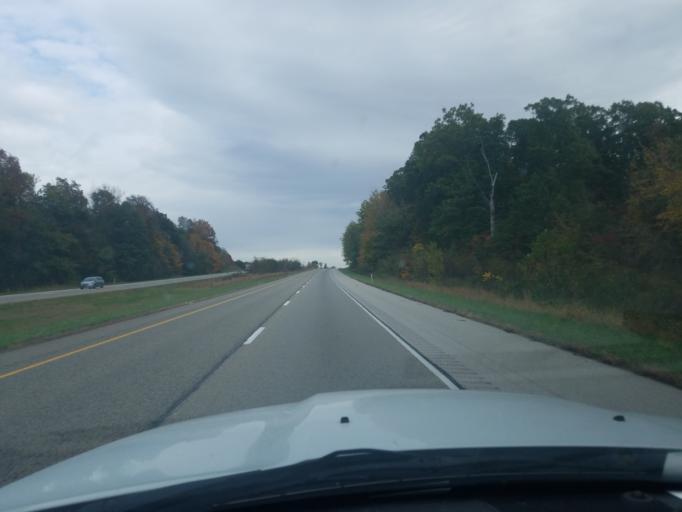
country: US
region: Indiana
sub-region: Spencer County
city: Dale
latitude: 38.1984
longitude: -87.1620
